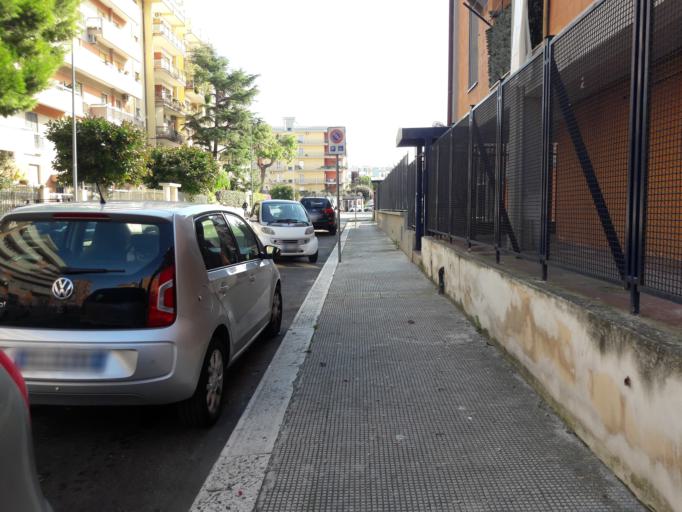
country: IT
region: Apulia
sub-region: Provincia di Bari
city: Bari
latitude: 41.1115
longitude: 16.8940
